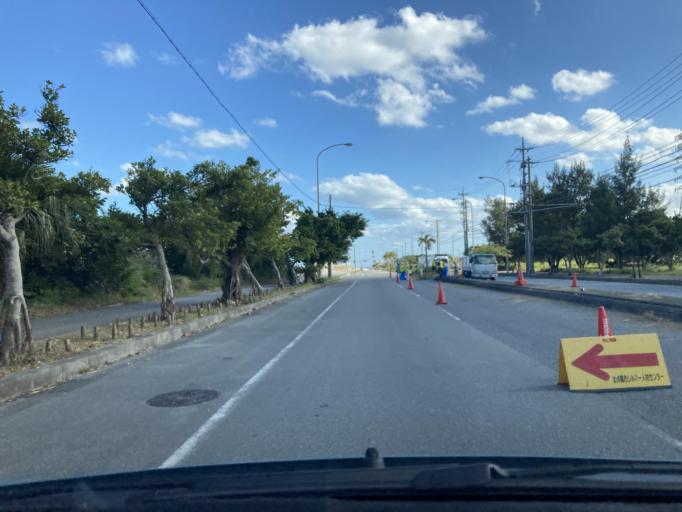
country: JP
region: Okinawa
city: Katsuren-haebaru
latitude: 26.3318
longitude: 127.8534
